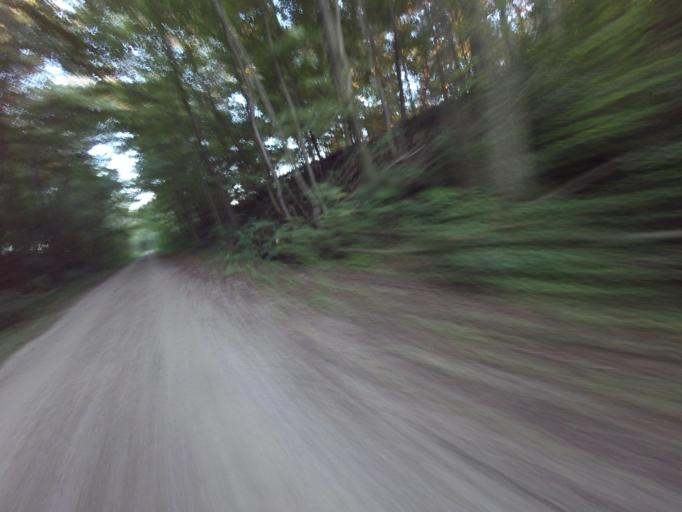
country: CA
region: Ontario
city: Goderich
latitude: 43.7479
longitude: -81.6455
